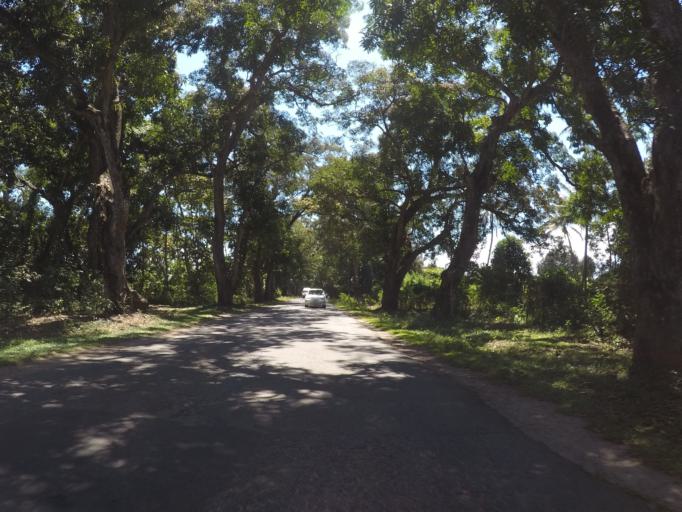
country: TZ
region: Zanzibar Central/South
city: Koani
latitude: -6.2576
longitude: 39.3382
